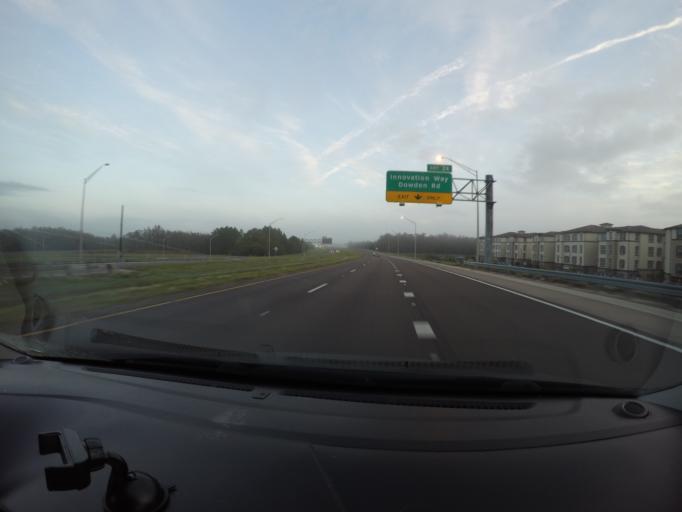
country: US
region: Florida
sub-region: Orange County
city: Conway
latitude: 28.4157
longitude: -81.2273
